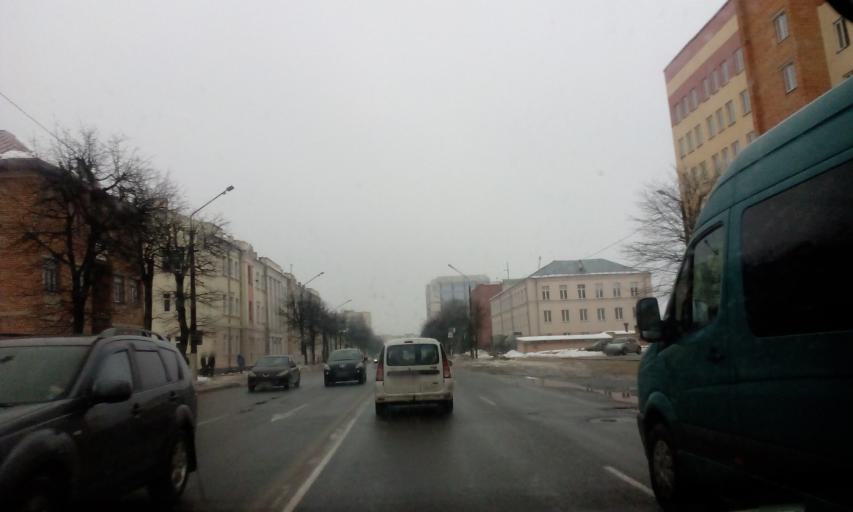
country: BY
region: Mogilev
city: Mahilyow
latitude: 53.8980
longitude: 30.3393
